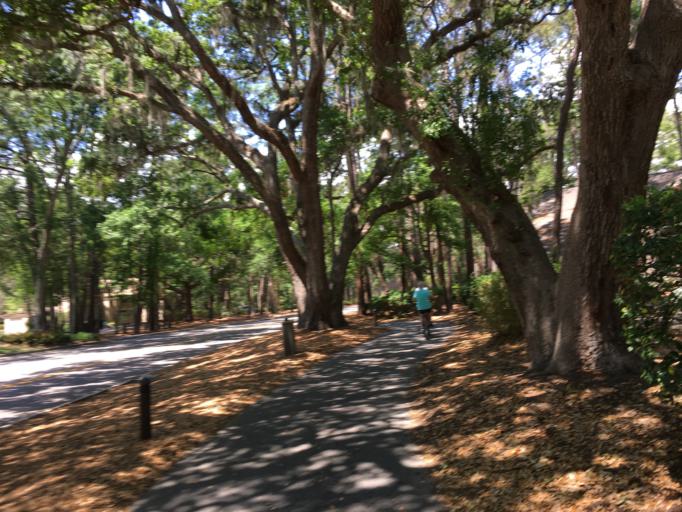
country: US
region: South Carolina
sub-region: Beaufort County
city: Hilton Head Island
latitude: 32.1322
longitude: -80.8010
